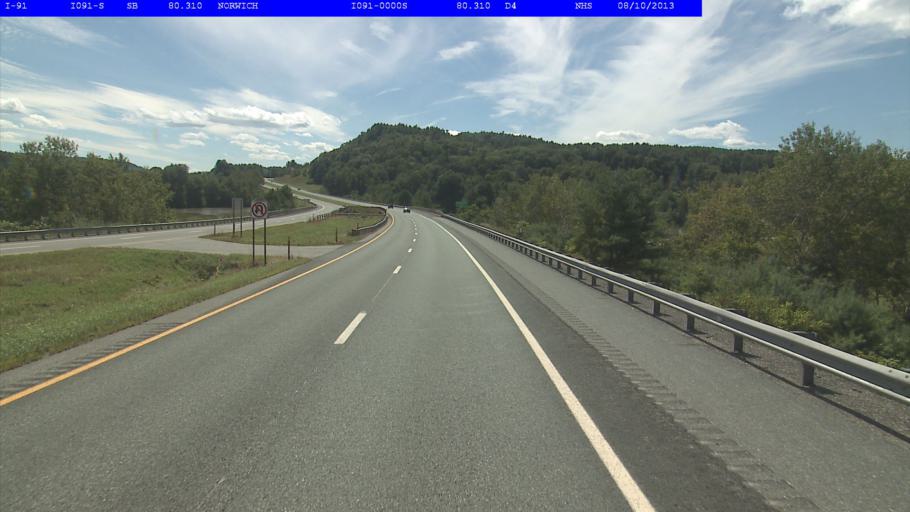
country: US
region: New Hampshire
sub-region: Grafton County
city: Hanover
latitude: 43.7610
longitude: -72.2314
